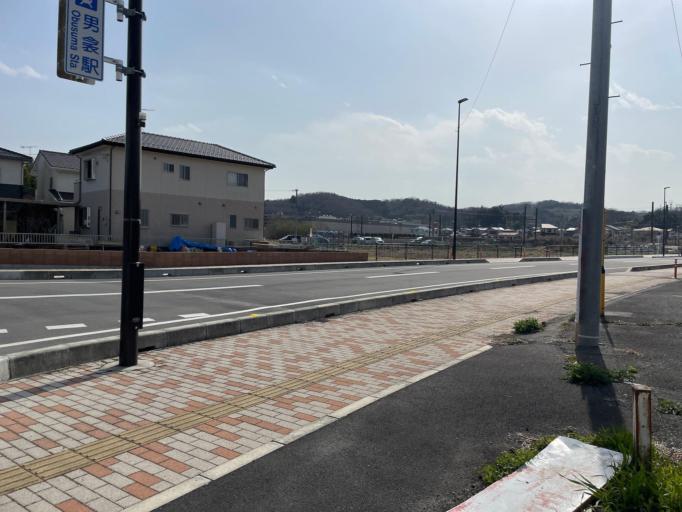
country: JP
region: Saitama
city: Yorii
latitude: 36.1074
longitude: 139.2358
